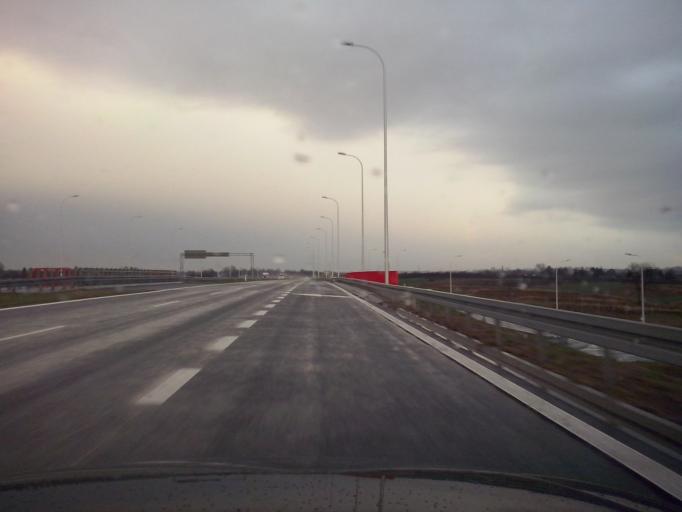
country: PL
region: Lublin Voivodeship
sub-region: Powiat lubelski
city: Jastkow
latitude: 51.2807
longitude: 22.4618
